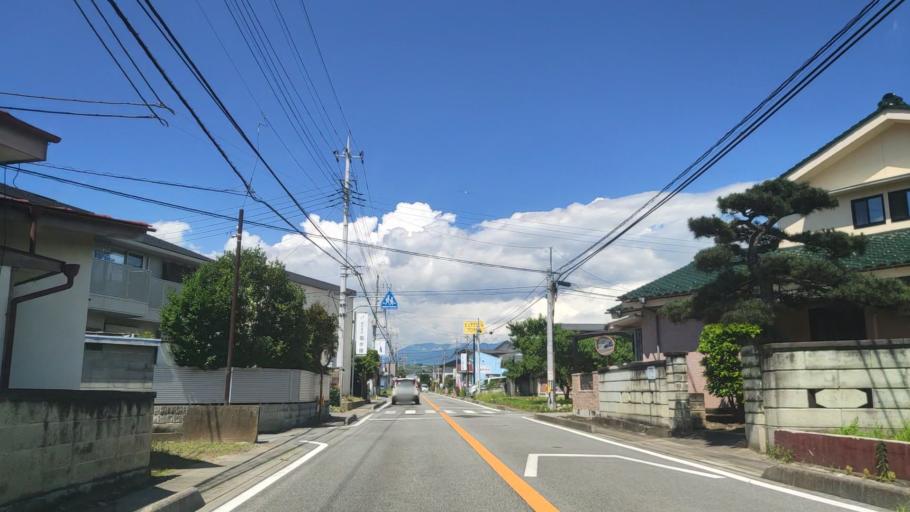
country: JP
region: Yamanashi
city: Isawa
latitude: 35.6680
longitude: 138.6477
